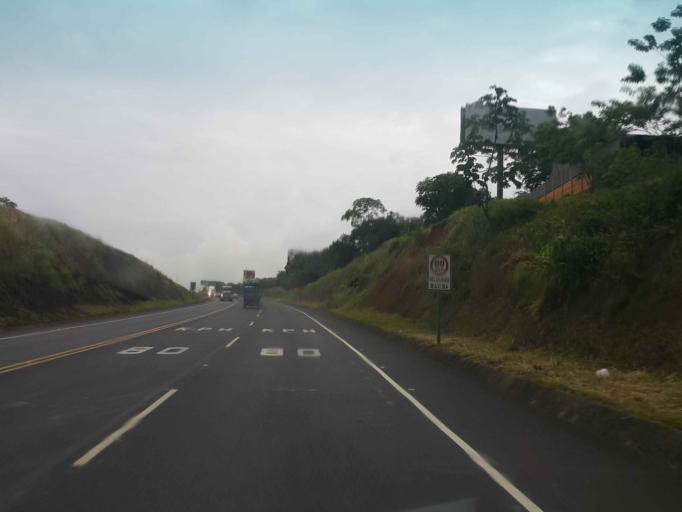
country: CR
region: Alajuela
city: Atenas
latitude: 9.9632
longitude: -84.3227
